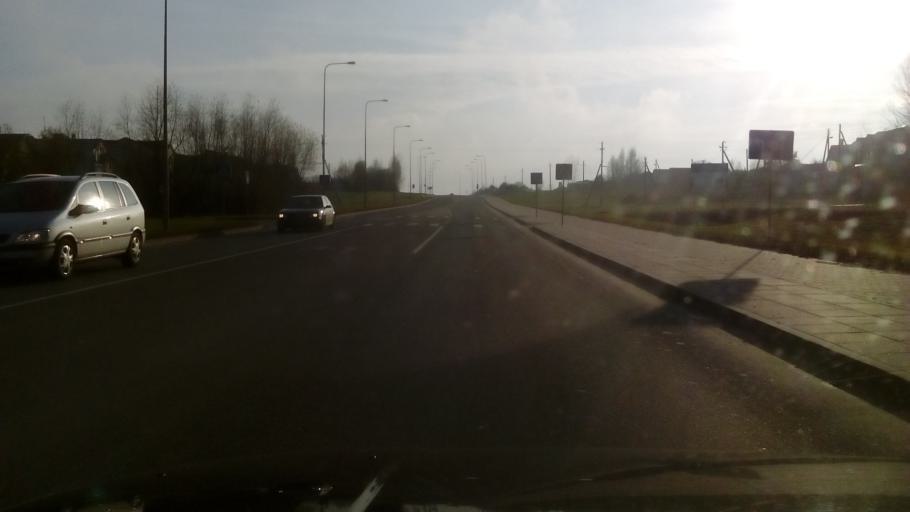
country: LT
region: Alytaus apskritis
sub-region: Alytus
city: Alytus
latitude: 54.3995
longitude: 24.0006
